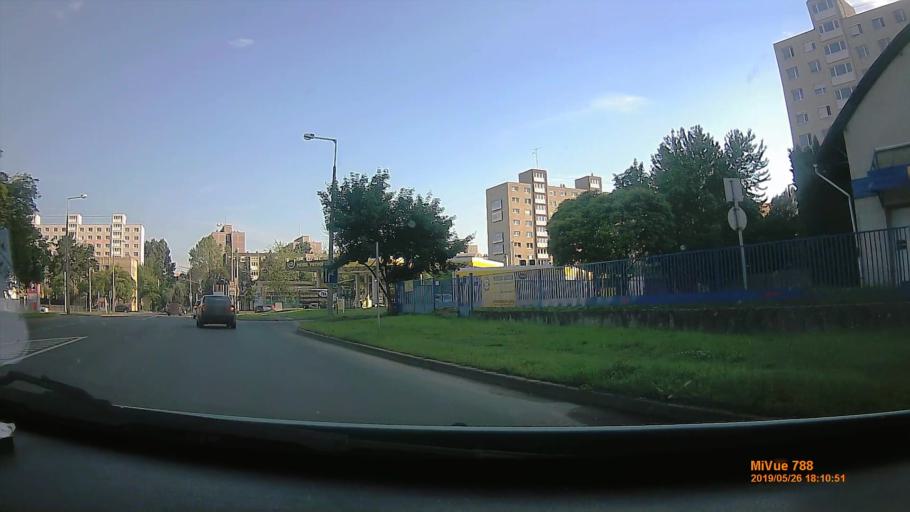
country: HU
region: Borsod-Abauj-Zemplen
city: Miskolc
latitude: 48.1049
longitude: 20.7572
